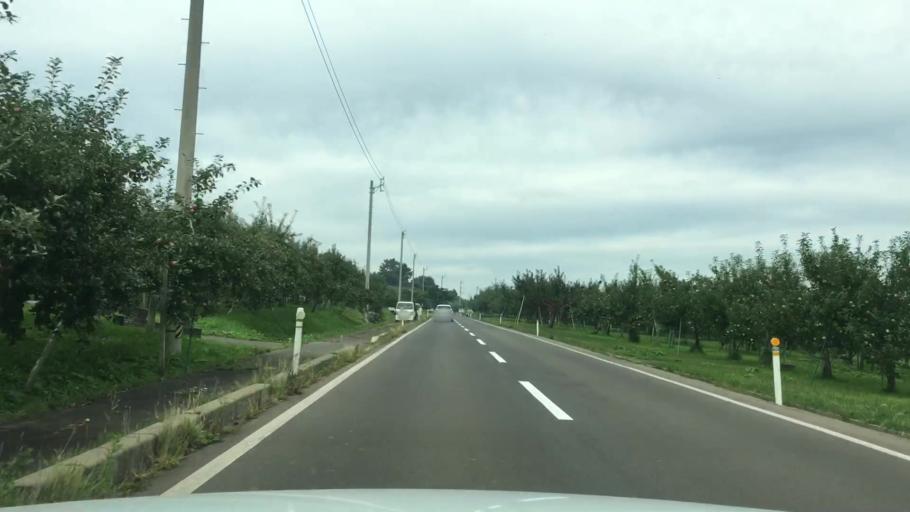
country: JP
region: Aomori
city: Hirosaki
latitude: 40.6703
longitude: 140.3879
